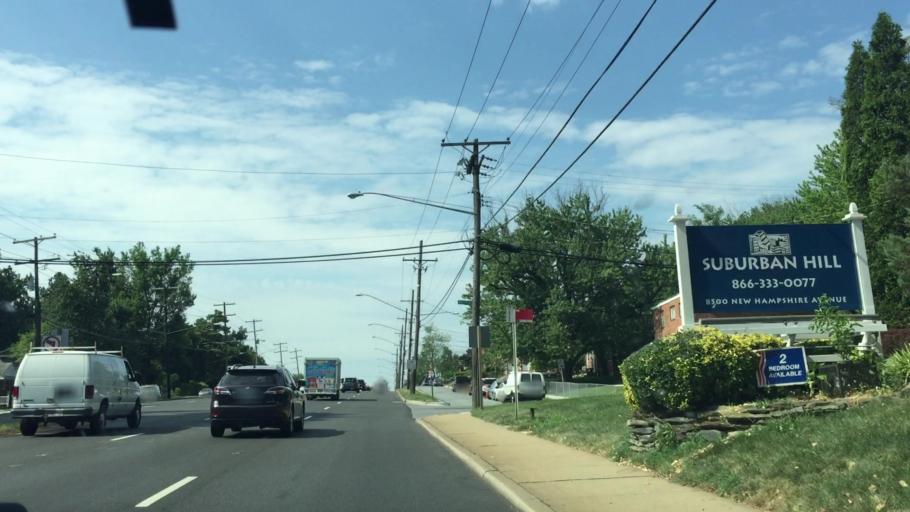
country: US
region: Maryland
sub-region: Prince George's County
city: Langley Park
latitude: 38.9996
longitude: -76.9832
